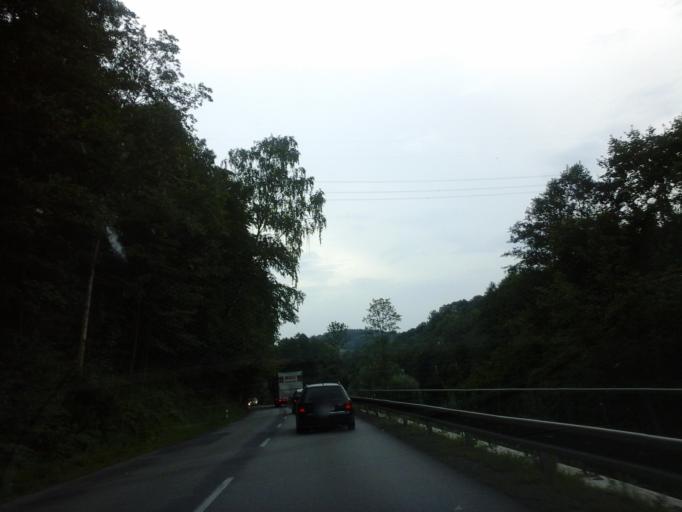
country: CZ
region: Pardubicky
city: Brnenec
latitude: 49.6081
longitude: 16.5317
